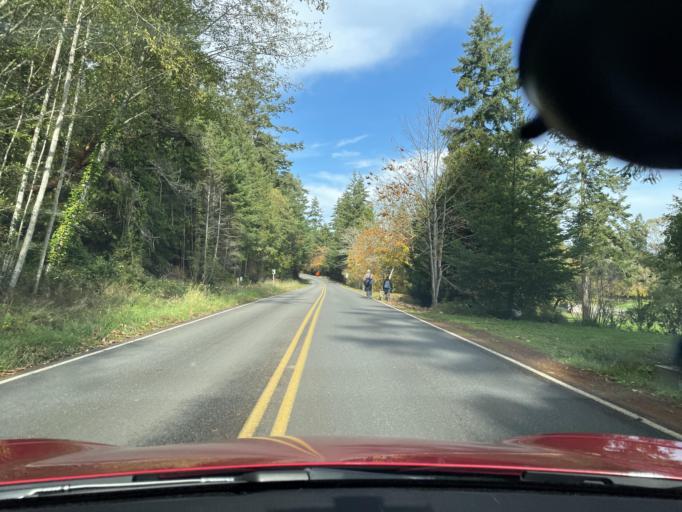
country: US
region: Washington
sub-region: San Juan County
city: Friday Harbor
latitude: 48.5292
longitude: -123.0050
